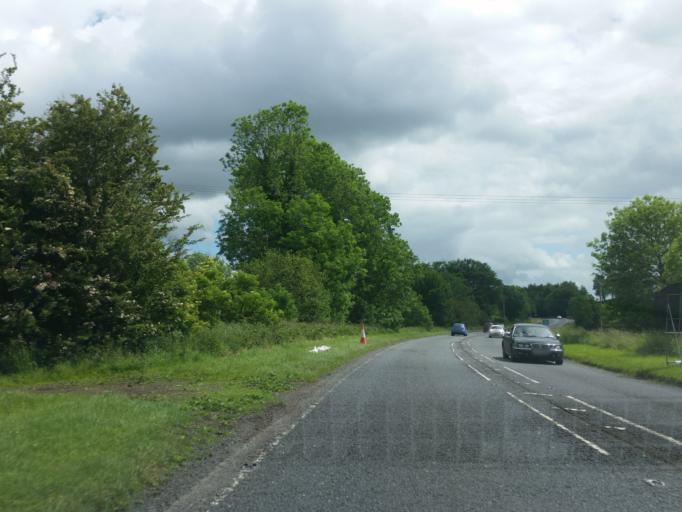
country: IE
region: Ulster
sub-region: County Monaghan
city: Monaghan
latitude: 54.4701
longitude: -7.0489
